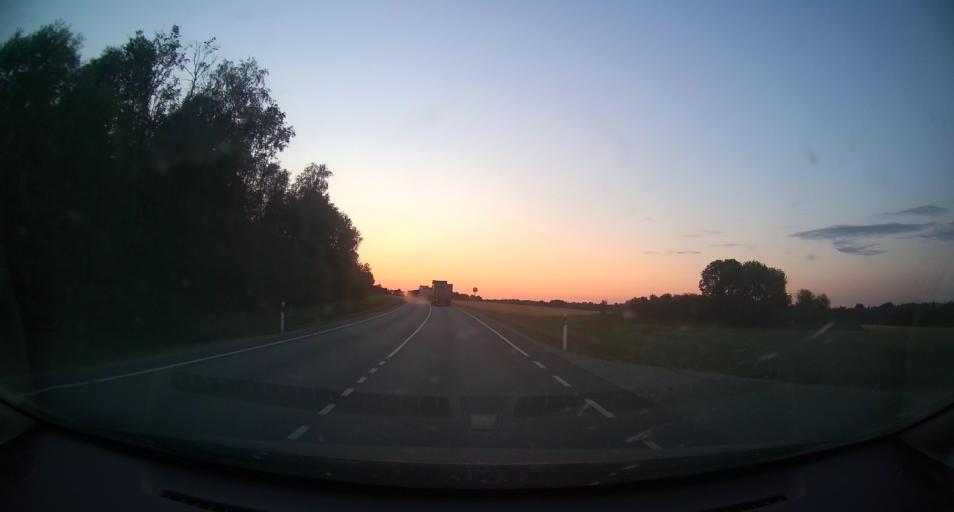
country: EE
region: Harju
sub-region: Anija vald
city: Kehra
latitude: 59.3902
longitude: 25.2727
